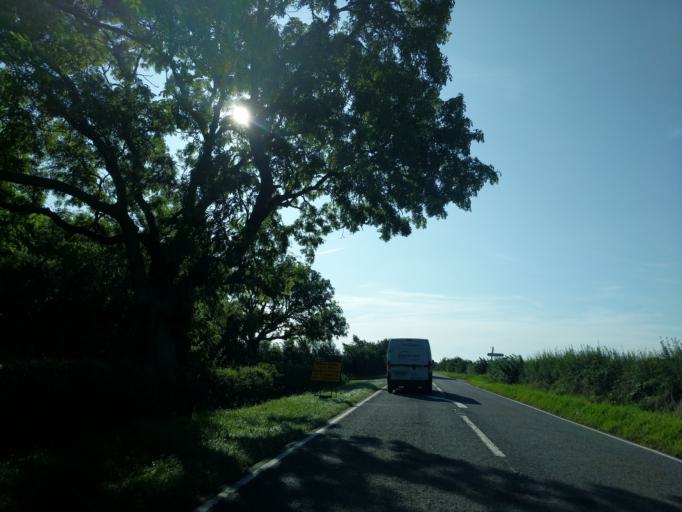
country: GB
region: England
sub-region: District of Rutland
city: Pickworth
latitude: 52.8053
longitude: -0.4819
